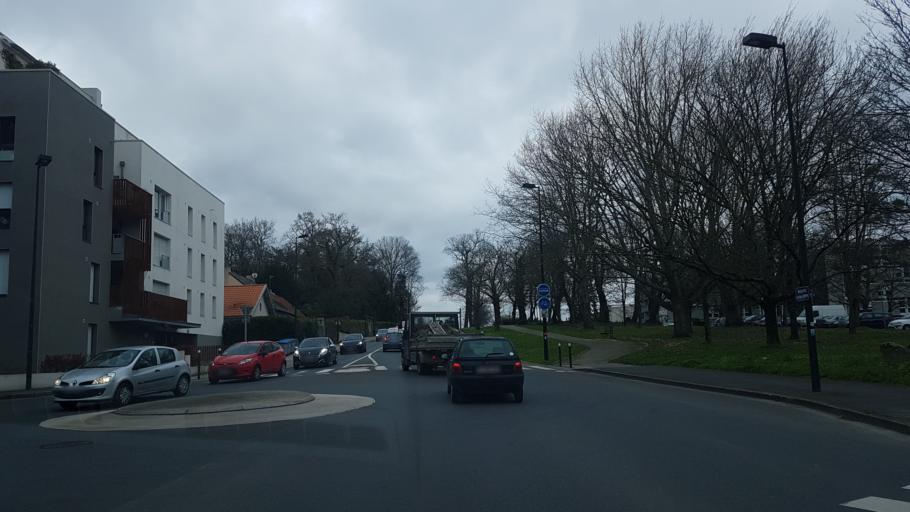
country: FR
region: Pays de la Loire
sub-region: Departement de la Loire-Atlantique
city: Nantes
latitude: 47.2502
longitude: -1.5299
